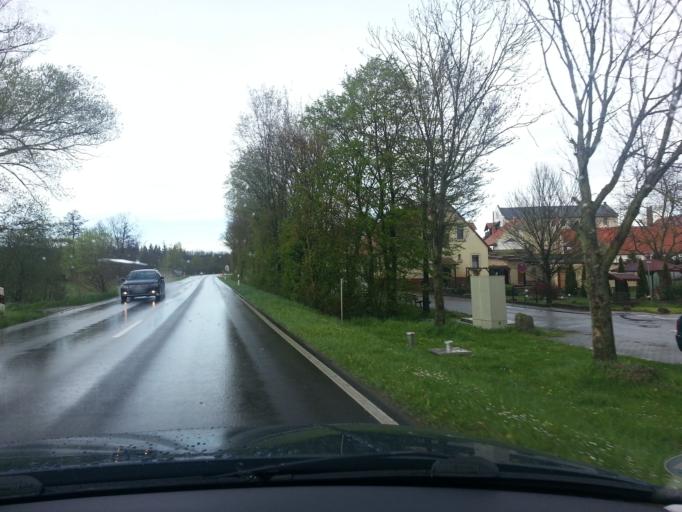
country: DE
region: Rheinland-Pfalz
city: Ottersheim
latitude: 49.2087
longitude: 8.2132
